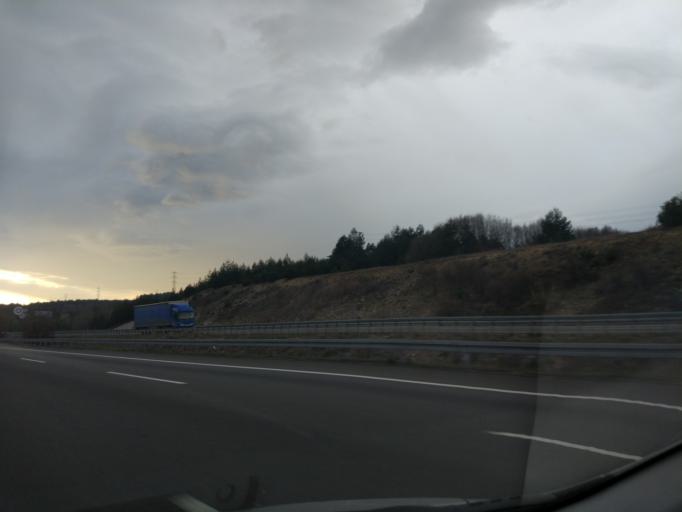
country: TR
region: Bolu
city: Yenicaga
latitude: 40.7521
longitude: 31.9046
